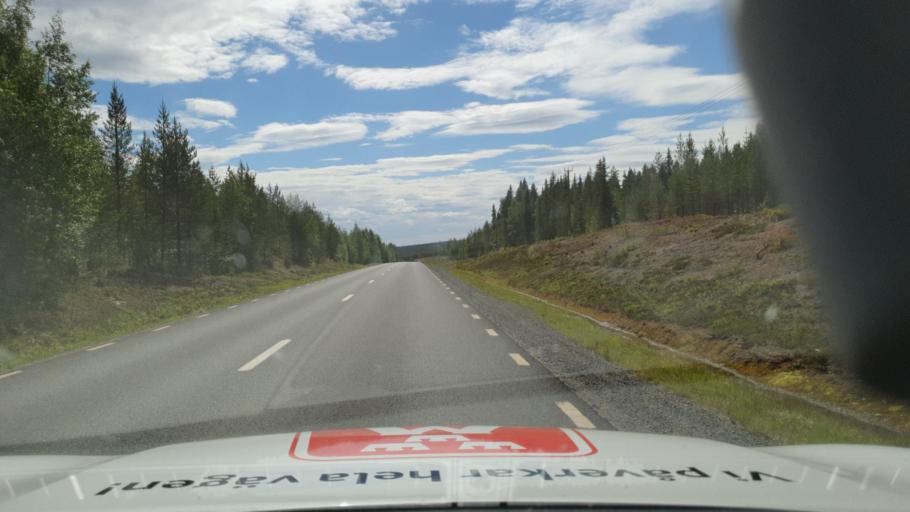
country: SE
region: Vaesterbotten
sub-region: Norsjo Kommun
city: Norsjoe
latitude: 65.1680
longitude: 19.5233
